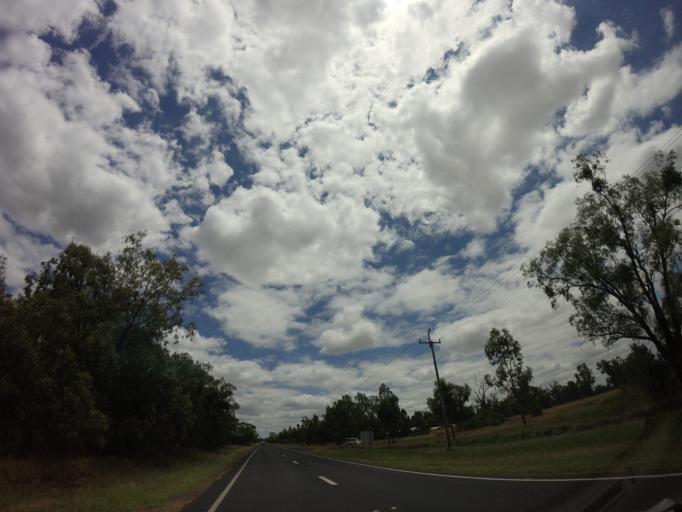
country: AU
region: New South Wales
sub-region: Moree Plains
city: Boggabilla
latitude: -28.5915
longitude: 150.3538
